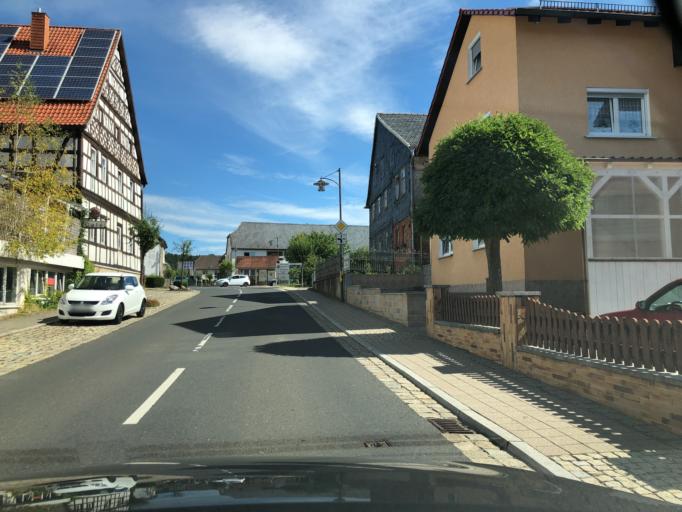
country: DE
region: Bavaria
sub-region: Upper Franconia
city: Sonnefeld
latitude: 50.2155
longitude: 11.0892
